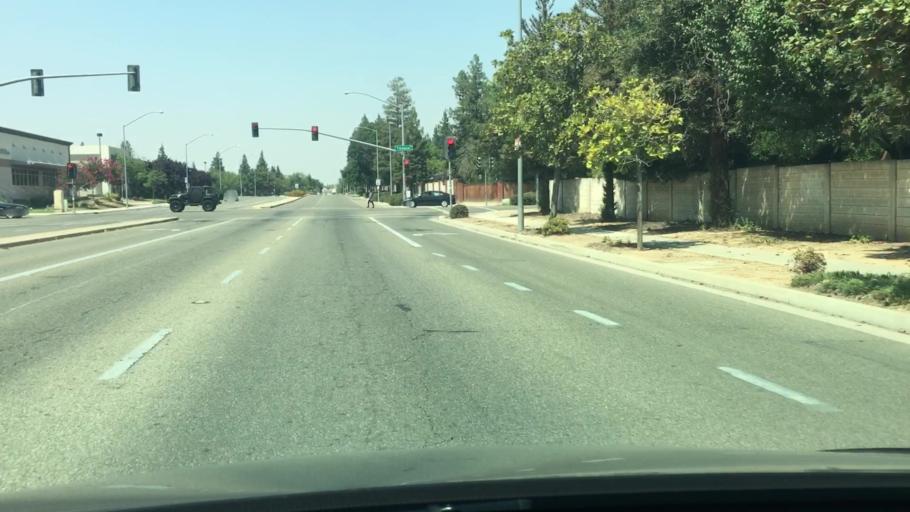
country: US
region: California
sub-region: Fresno County
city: Clovis
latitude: 36.8587
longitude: -119.7567
